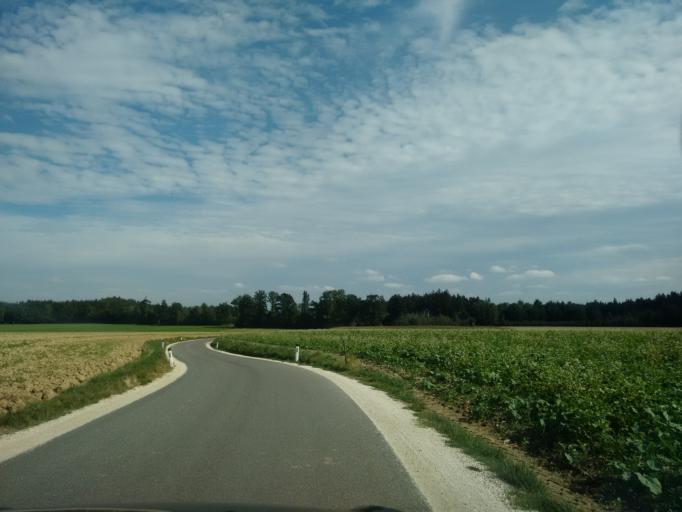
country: AT
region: Upper Austria
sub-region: Politischer Bezirk Kirchdorf an der Krems
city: Kremsmunster
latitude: 48.1176
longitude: 14.1412
